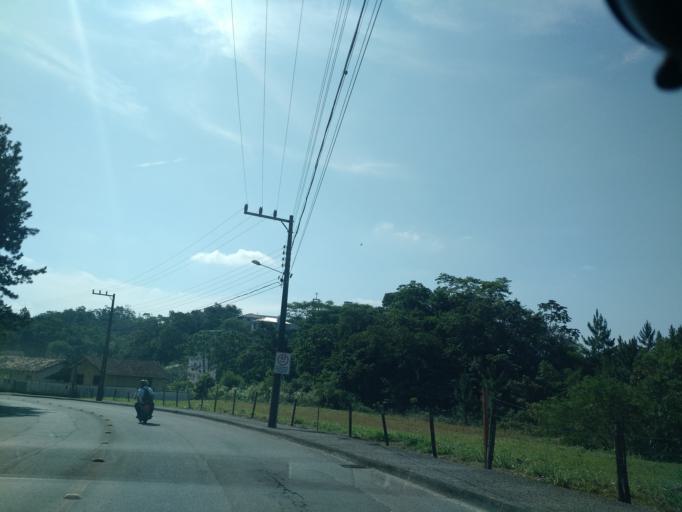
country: BR
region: Santa Catarina
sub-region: Jaragua Do Sul
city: Jaragua do Sul
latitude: -26.4963
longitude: -49.0999
